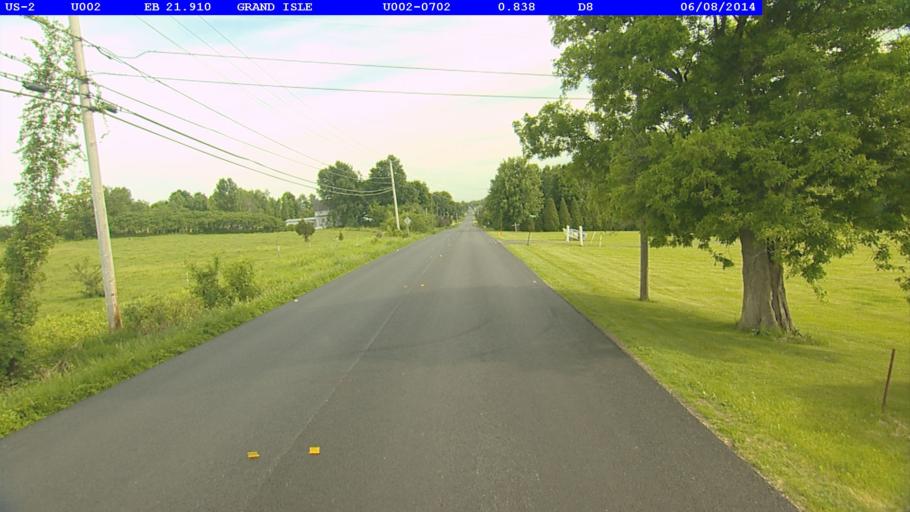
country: US
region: Vermont
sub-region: Grand Isle County
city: North Hero
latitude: 44.7552
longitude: -73.2867
